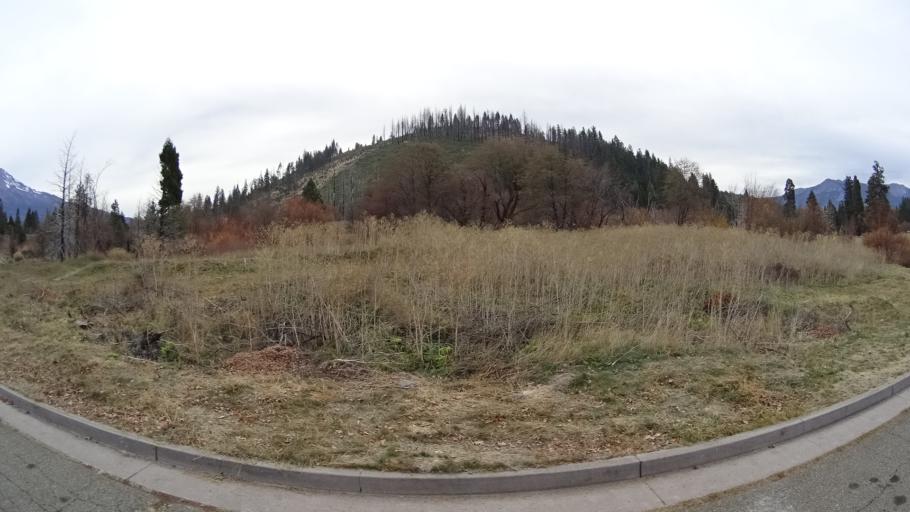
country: US
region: California
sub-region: Siskiyou County
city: Weed
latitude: 41.4217
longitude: -122.3797
